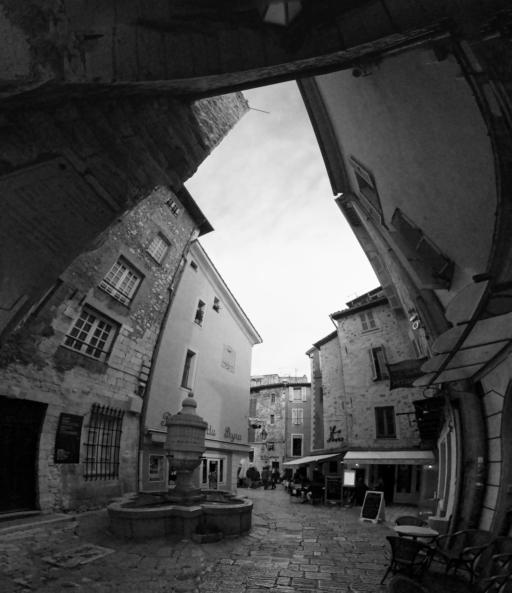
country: FR
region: Provence-Alpes-Cote d'Azur
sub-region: Departement des Alpes-Maritimes
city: Vence
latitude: 43.7228
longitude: 7.1124
